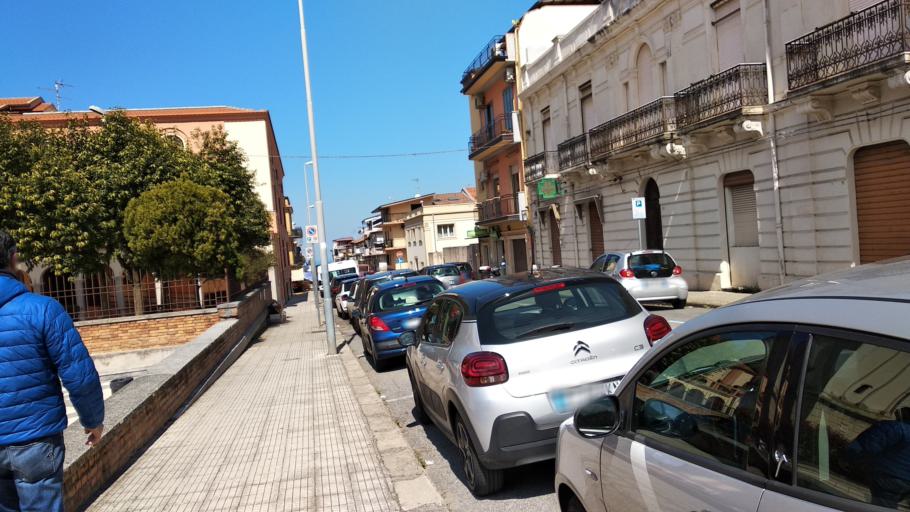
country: IT
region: Calabria
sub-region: Provincia di Reggio Calabria
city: Seminara
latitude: 38.3593
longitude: 15.8494
